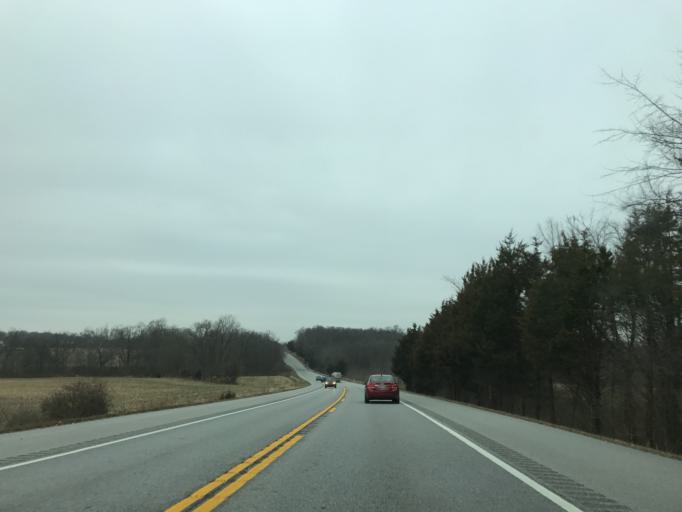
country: US
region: Maryland
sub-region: Carroll County
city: Taneytown
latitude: 39.6463
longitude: -77.1341
